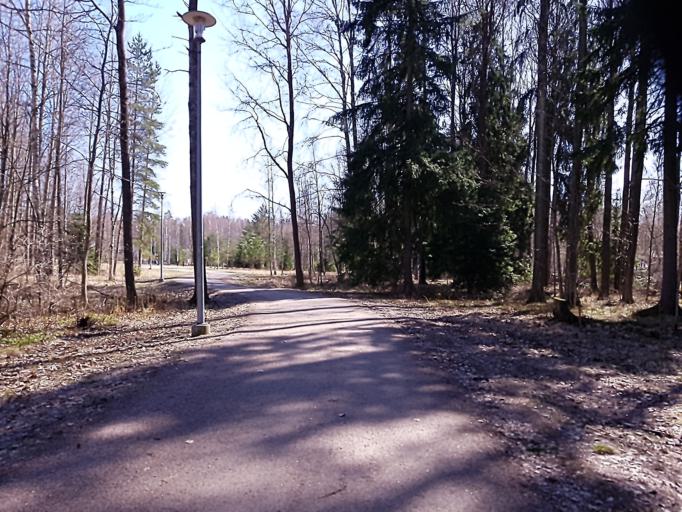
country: FI
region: Uusimaa
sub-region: Helsinki
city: Teekkarikylae
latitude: 60.2680
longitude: 24.8850
